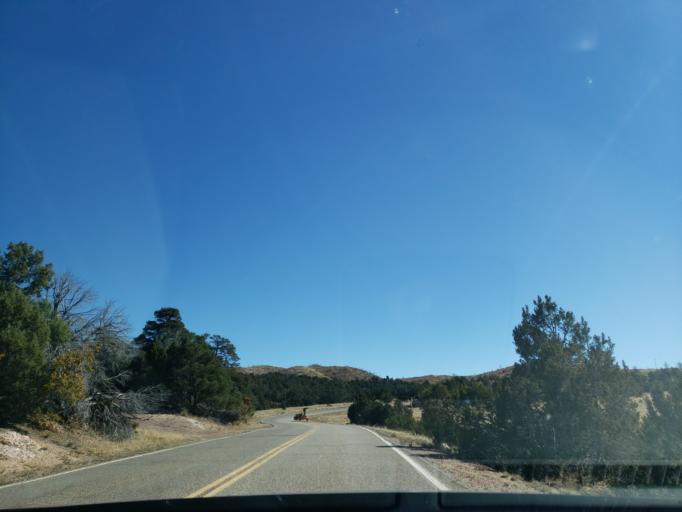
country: US
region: Colorado
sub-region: Fremont County
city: Canon City
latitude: 38.4765
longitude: -105.3095
